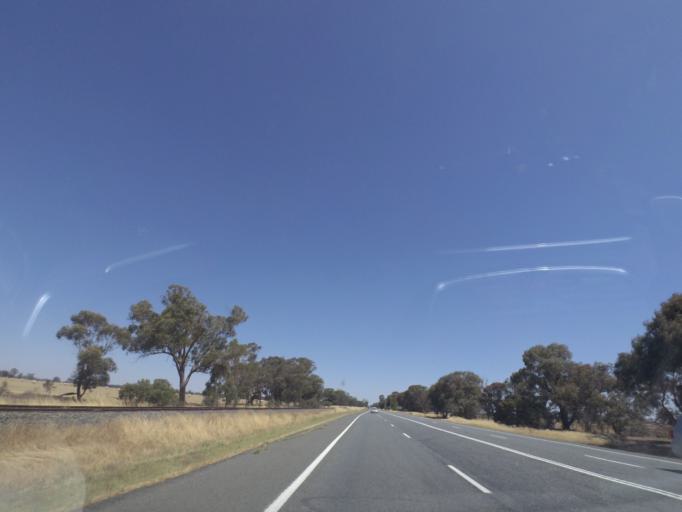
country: AU
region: Victoria
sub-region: Greater Shepparton
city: Shepparton
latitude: -36.1942
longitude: 145.4319
